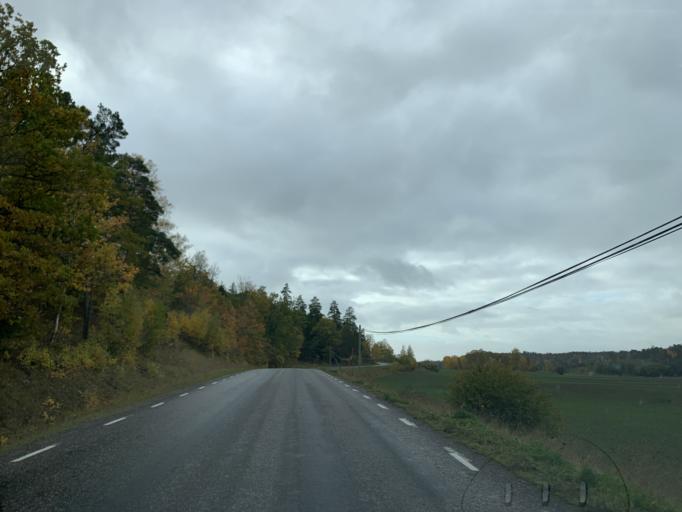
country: SE
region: Stockholm
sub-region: Nynashamns Kommun
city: Osmo
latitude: 58.9501
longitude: 17.7654
